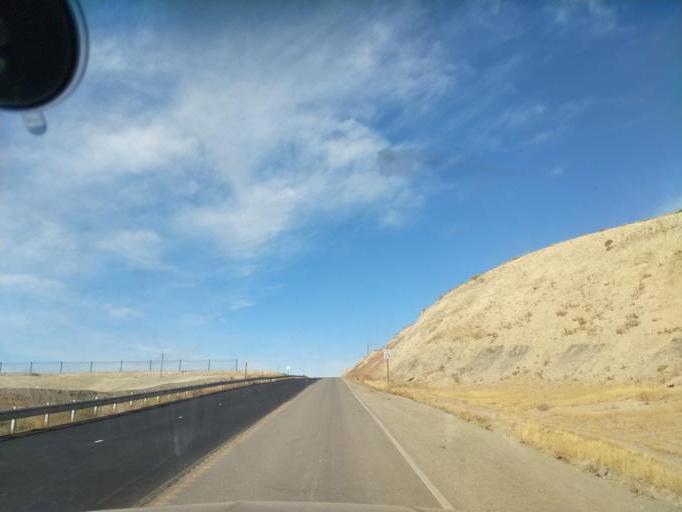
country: US
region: Colorado
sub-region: Mesa County
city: Fruitvale
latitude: 39.0121
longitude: -108.4844
